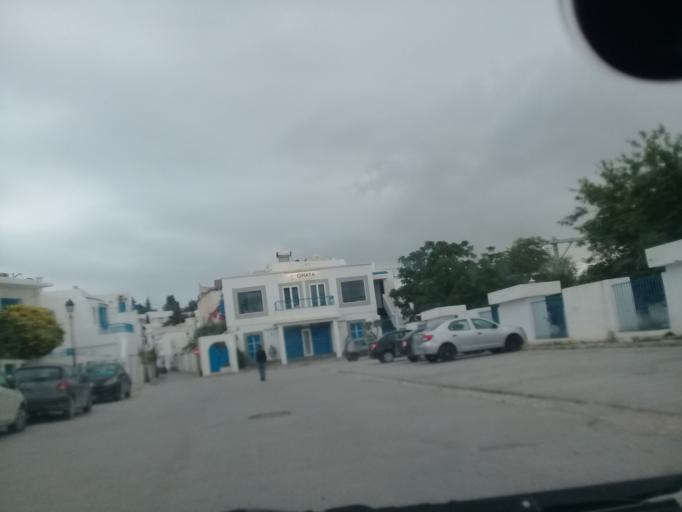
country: TN
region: Tunis
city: Sidi Bou Said
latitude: 36.8707
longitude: 10.3424
